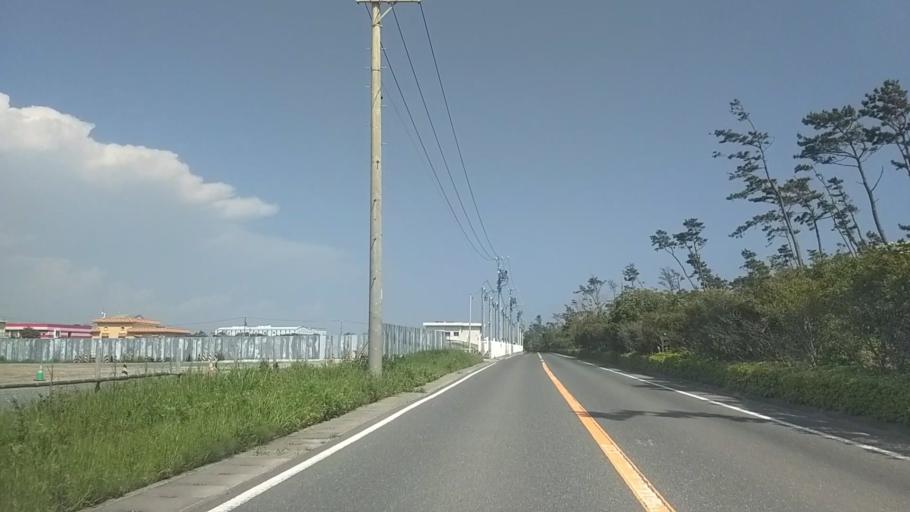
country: JP
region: Shizuoka
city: Hamamatsu
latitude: 34.6692
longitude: 137.6997
